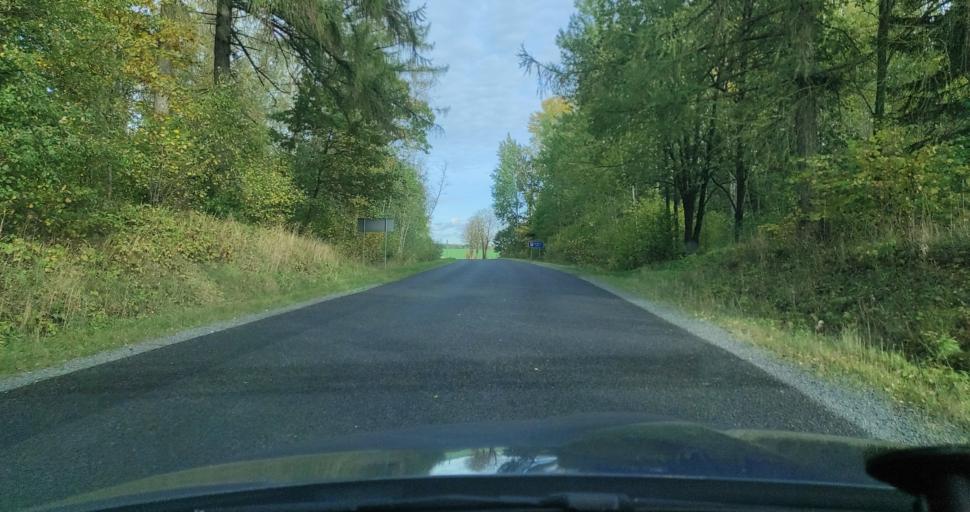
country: LV
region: Jaunpils
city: Jaunpils
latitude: 56.7166
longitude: 23.0026
